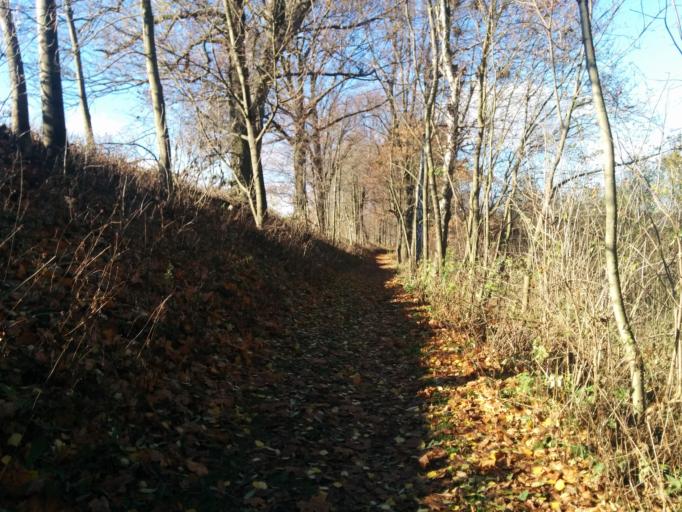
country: CZ
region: Vysocina
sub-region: Okres Jihlava
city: Jihlava
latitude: 49.4098
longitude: 15.5563
